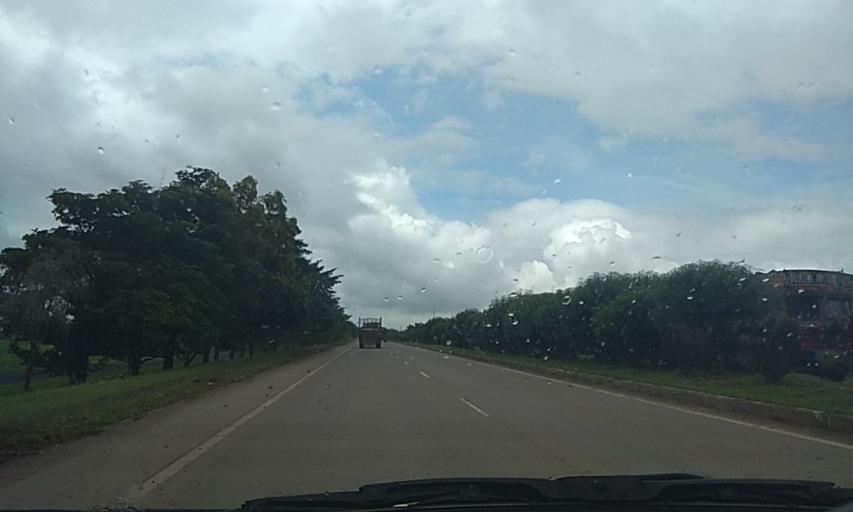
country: IN
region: Karnataka
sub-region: Belgaum
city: Sankeshwar
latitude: 16.3005
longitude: 74.4348
